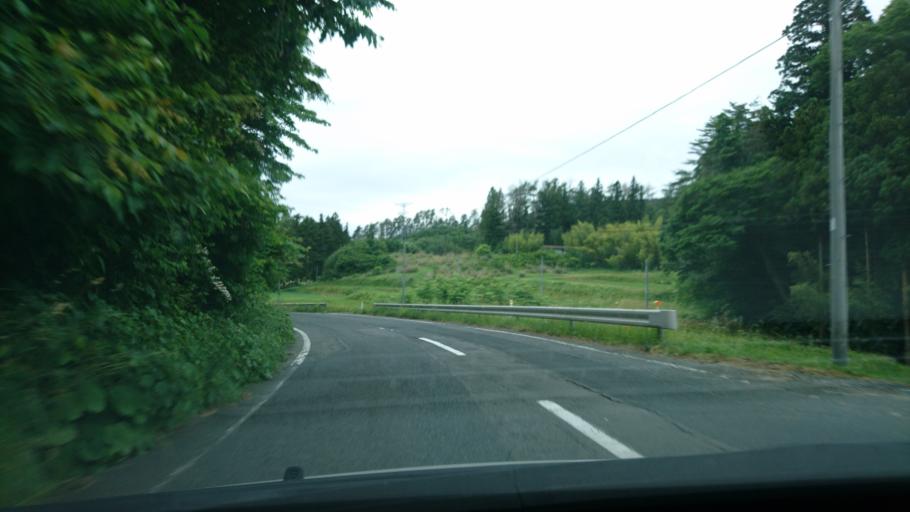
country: JP
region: Iwate
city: Ichinoseki
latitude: 38.9466
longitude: 141.2697
